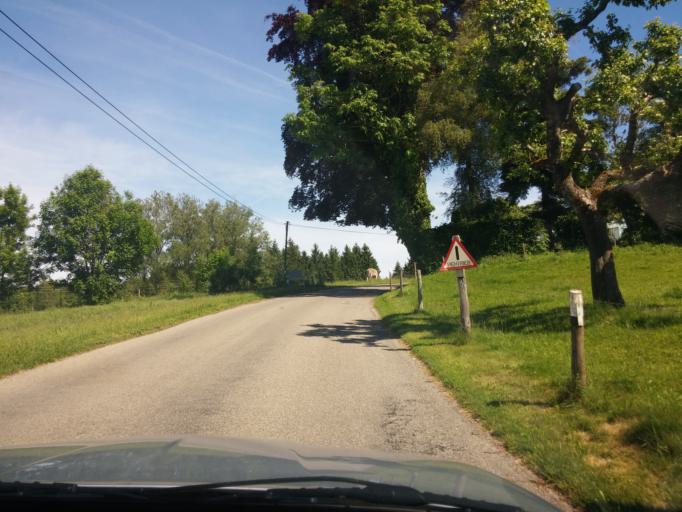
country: DE
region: Bavaria
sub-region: Swabia
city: Woringen
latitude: 47.8994
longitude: 10.1818
